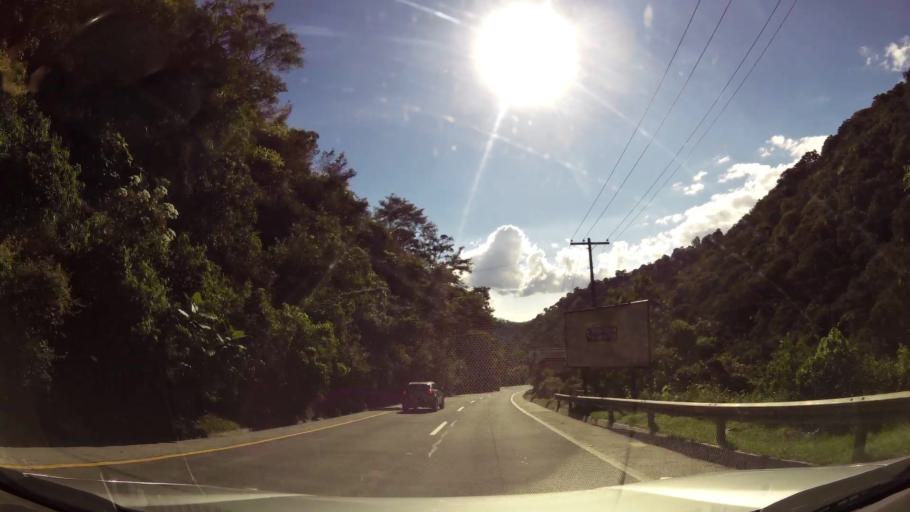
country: GT
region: Sacatepequez
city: Santa Lucia Milpas Altas
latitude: 14.5716
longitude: -90.6892
